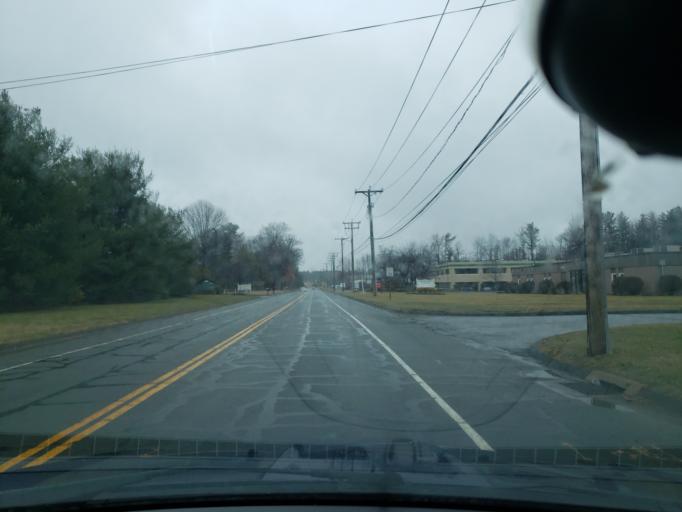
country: US
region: Connecticut
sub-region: Hartford County
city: Windsor
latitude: 41.8648
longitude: -72.6852
